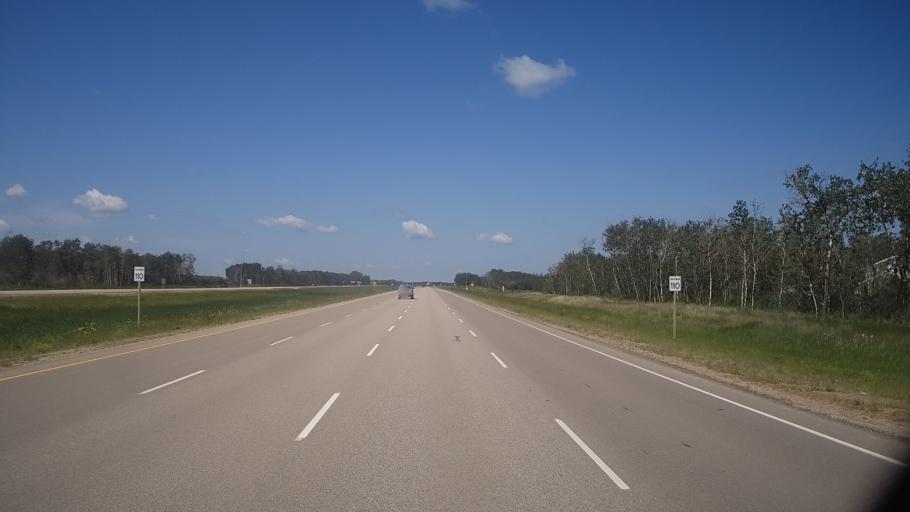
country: CA
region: Saskatchewan
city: Saskatoon
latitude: 52.0123
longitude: -106.3892
